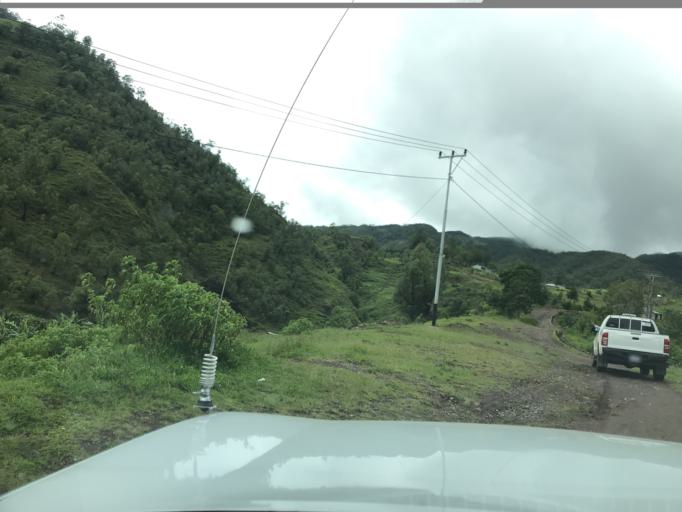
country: TL
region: Aileu
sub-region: Aileu Villa
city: Aileu
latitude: -8.8636
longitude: 125.5583
